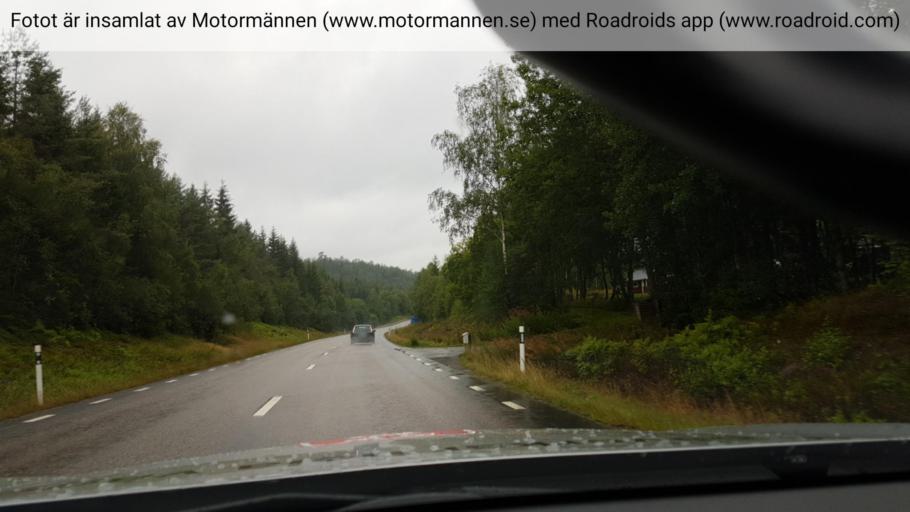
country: SE
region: Vaestra Goetaland
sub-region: Dals-Ed Kommun
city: Ed
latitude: 58.8762
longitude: 11.8733
